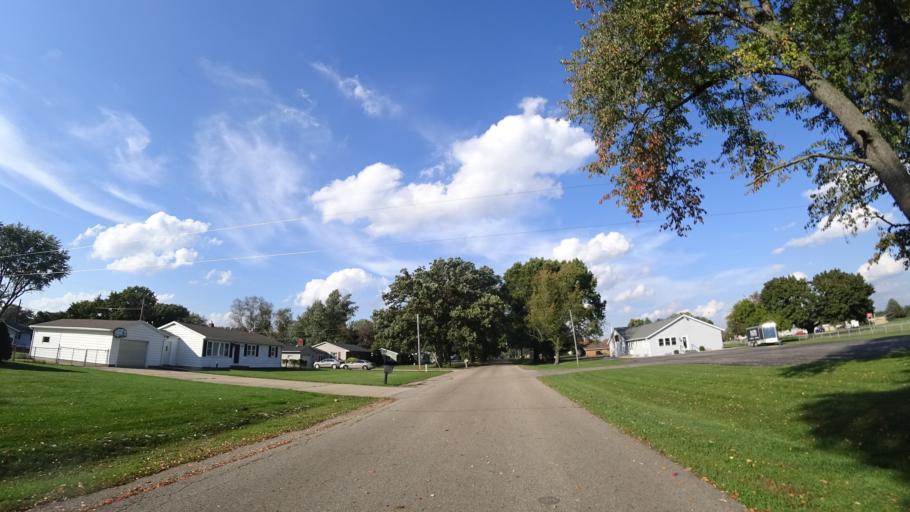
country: US
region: Michigan
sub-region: Saint Joseph County
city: Three Rivers
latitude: 41.9472
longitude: -85.6515
